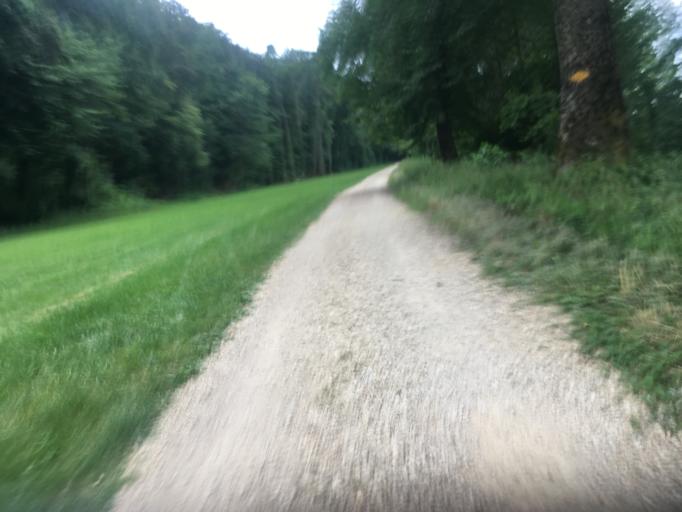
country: CH
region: Bern
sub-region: Jura bernois
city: La Neuveville
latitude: 47.0748
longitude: 7.1423
